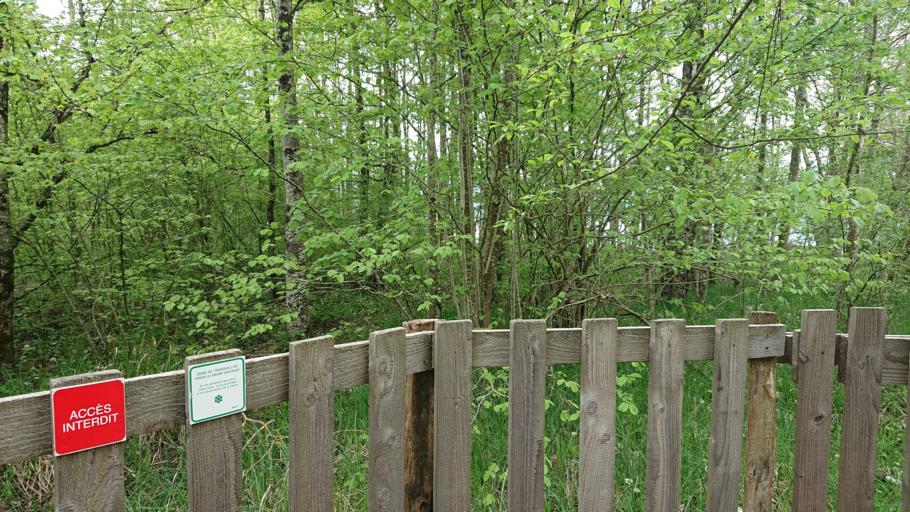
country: FR
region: Rhone-Alpes
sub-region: Departement de la Haute-Savoie
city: Doussard
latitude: 45.7939
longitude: 6.2226
